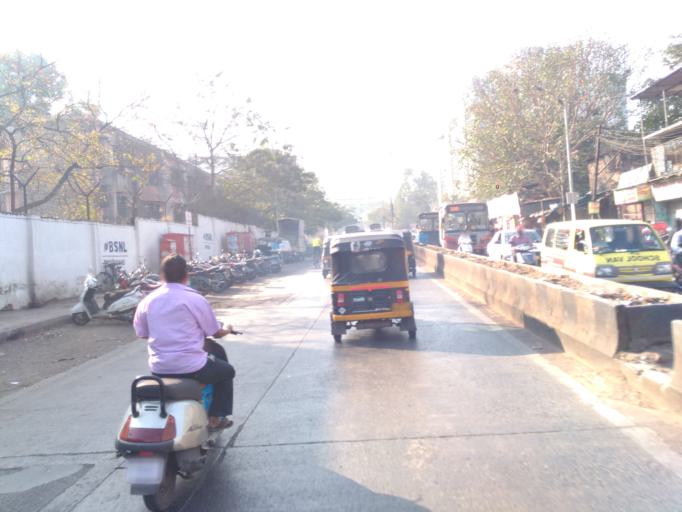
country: IN
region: Maharashtra
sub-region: Pune Division
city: Pune
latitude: 18.4939
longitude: 73.8693
